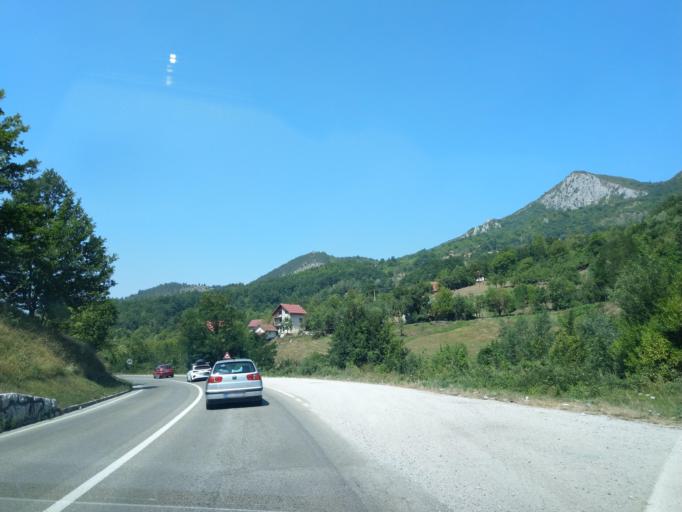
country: RS
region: Central Serbia
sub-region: Zlatiborski Okrug
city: Prijepolje
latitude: 43.4670
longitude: 19.6712
